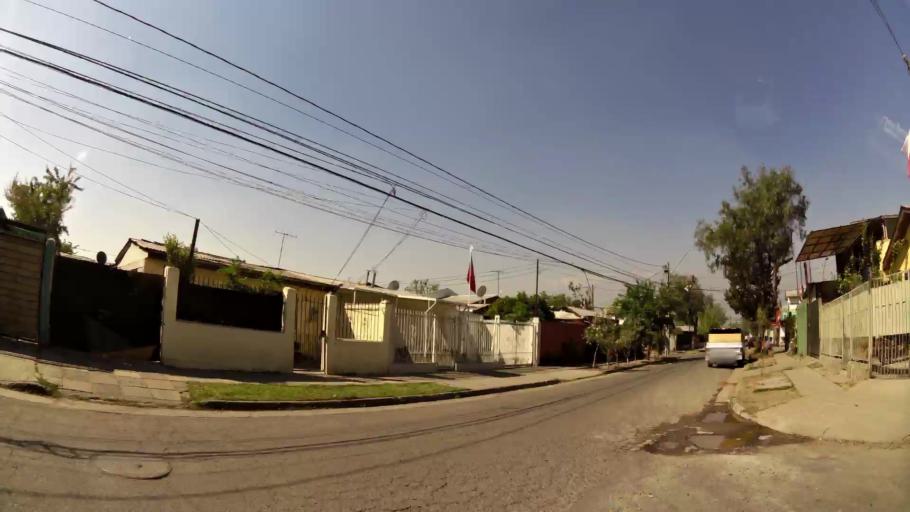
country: CL
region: Santiago Metropolitan
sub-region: Provincia de Santiago
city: La Pintana
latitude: -33.5414
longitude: -70.6090
